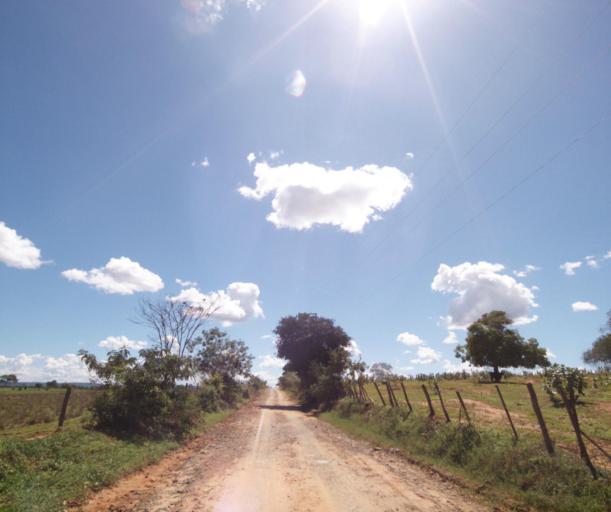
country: BR
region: Bahia
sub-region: Carinhanha
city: Carinhanha
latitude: -14.2178
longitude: -44.2883
